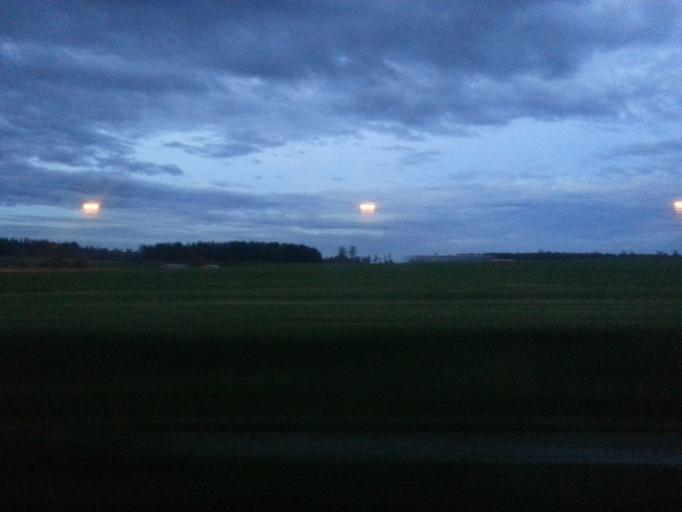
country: NO
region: Akershus
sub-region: Ullensaker
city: Jessheim
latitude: 60.1160
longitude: 11.1540
